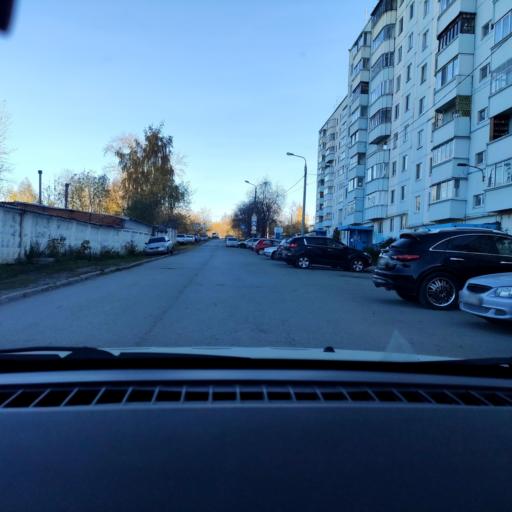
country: RU
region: Perm
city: Perm
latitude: 58.1141
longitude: 56.3745
